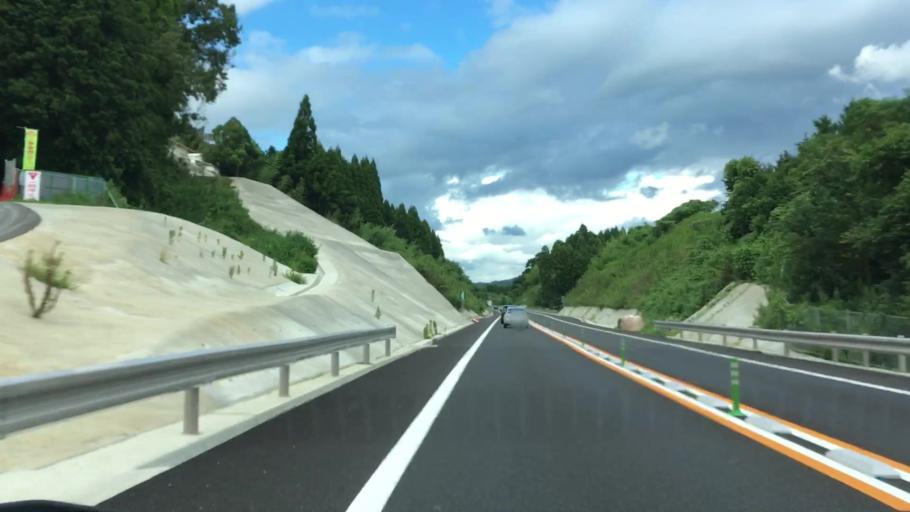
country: JP
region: Saga Prefecture
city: Imaricho-ko
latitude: 33.3154
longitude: 129.9207
